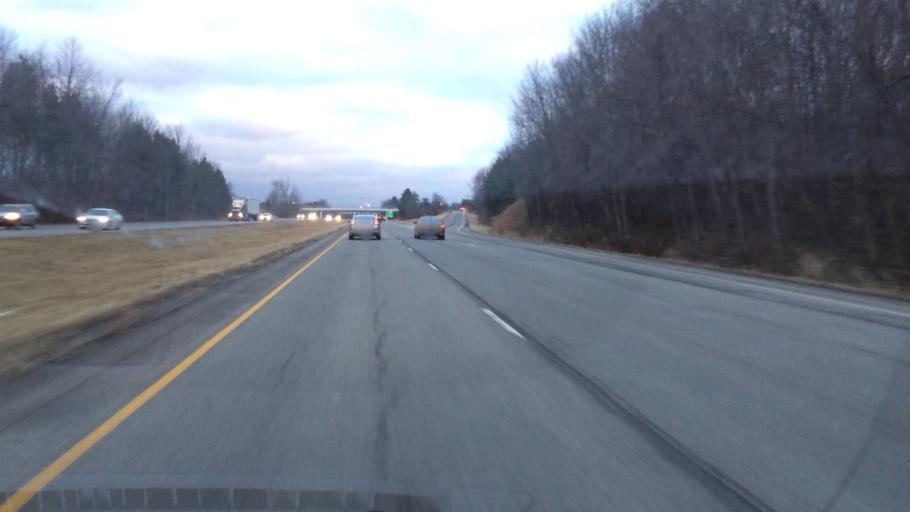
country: US
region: Ohio
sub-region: Summit County
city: Norton
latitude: 41.0542
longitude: -81.6623
